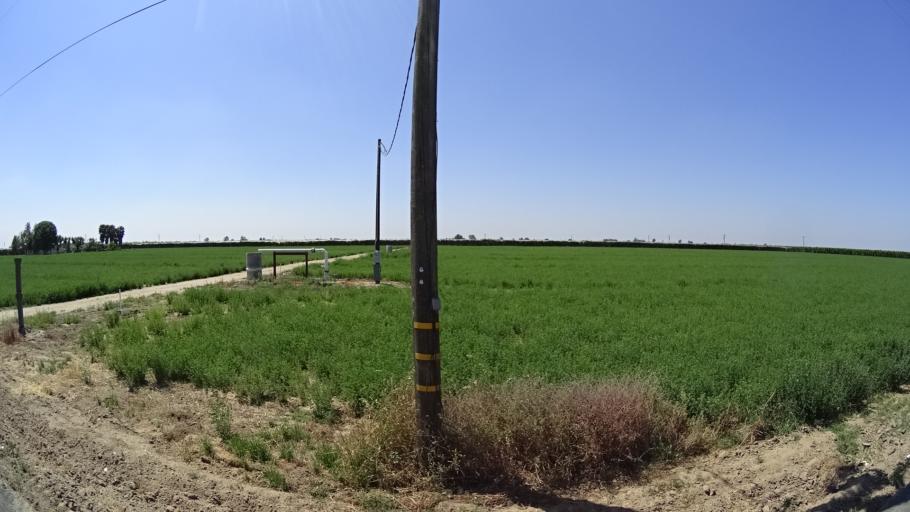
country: US
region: California
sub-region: Fresno County
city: Kingsburg
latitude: 36.4743
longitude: -119.5979
